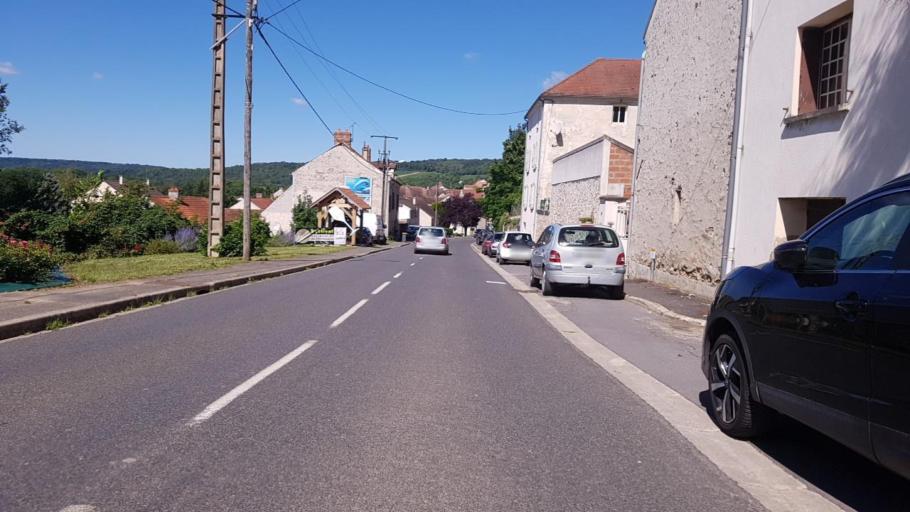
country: FR
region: Ile-de-France
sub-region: Departement de Seine-et-Marne
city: Saacy-sur-Marne
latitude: 48.9791
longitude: 3.2436
